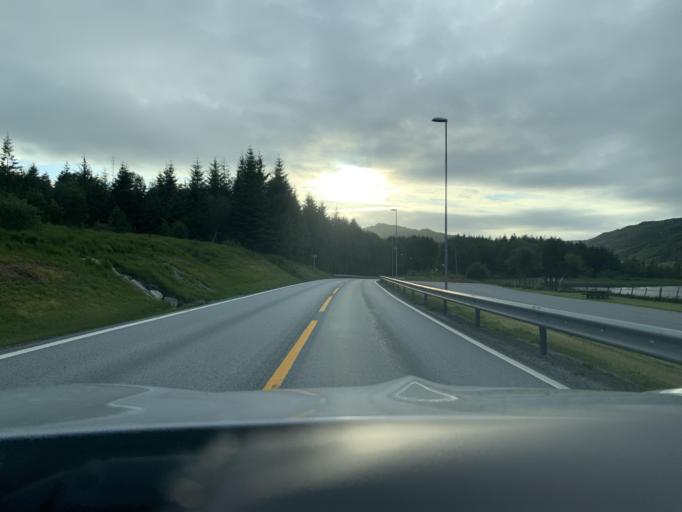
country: NO
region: Rogaland
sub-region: Bjerkreim
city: Vikesa
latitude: 58.6444
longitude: 6.0524
